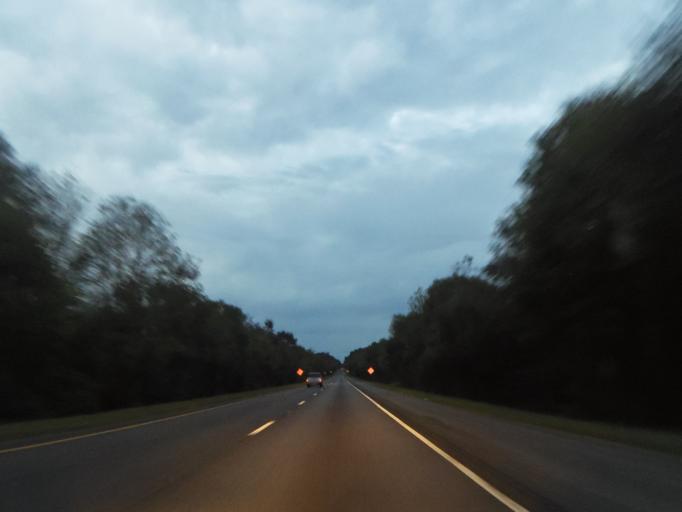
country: US
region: Alabama
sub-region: DeKalb County
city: Crossville
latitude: 34.1958
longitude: -85.9474
